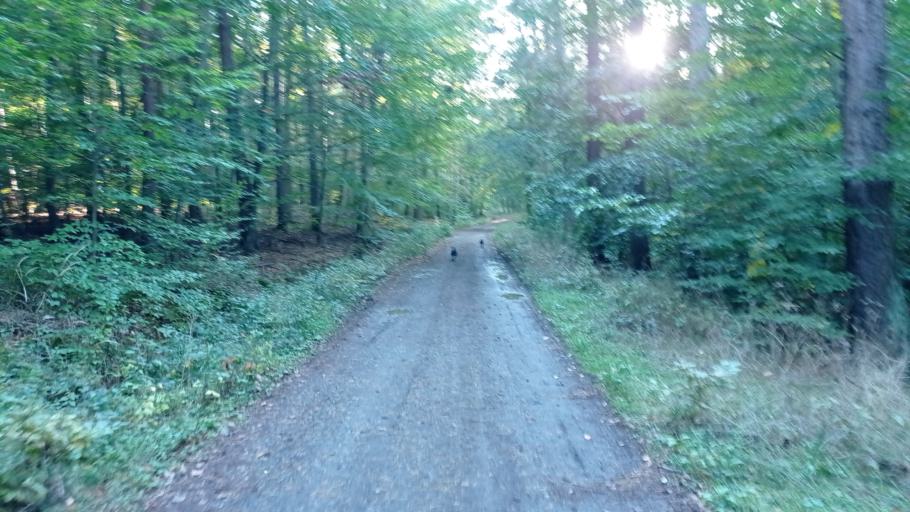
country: CZ
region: Central Bohemia
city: Chynava
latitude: 50.0554
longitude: 14.0508
